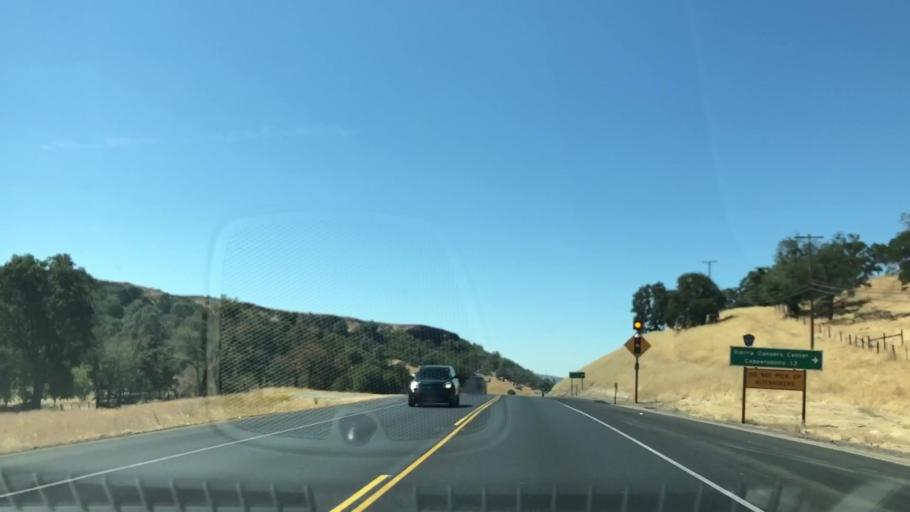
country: US
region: California
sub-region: Tuolumne County
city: Jamestown
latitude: 37.8873
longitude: -120.4968
